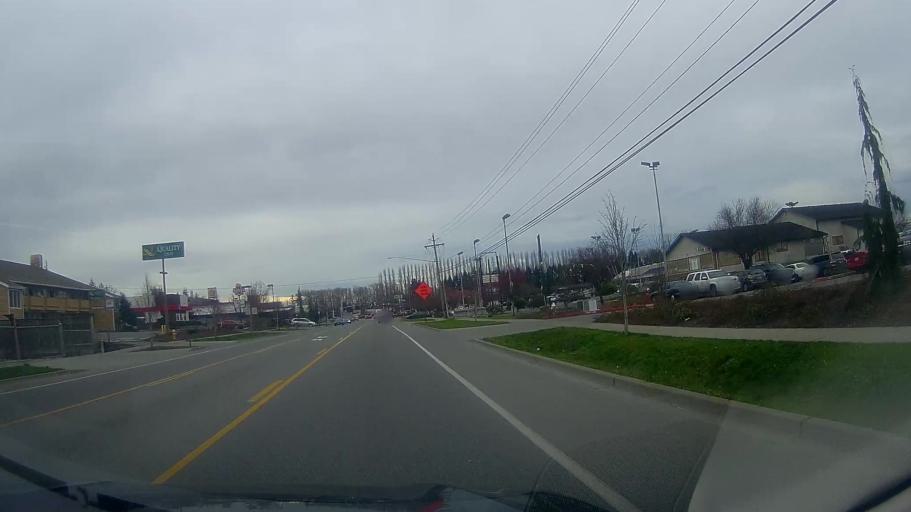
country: US
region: Washington
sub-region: Skagit County
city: Mount Vernon
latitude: 48.4386
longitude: -122.3432
